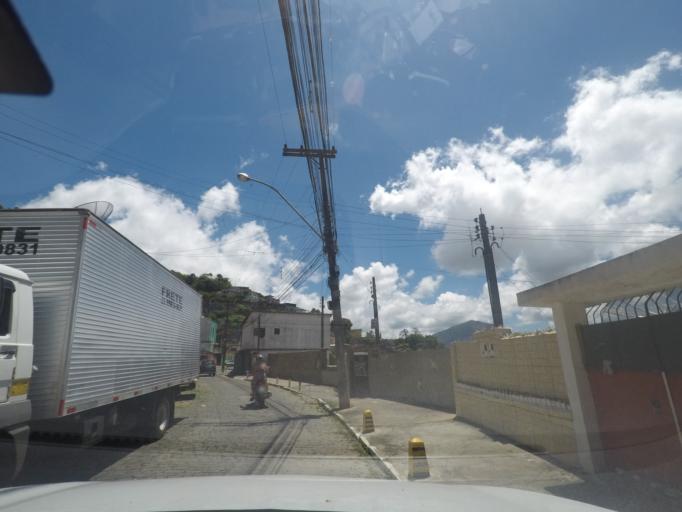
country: BR
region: Rio de Janeiro
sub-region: Teresopolis
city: Teresopolis
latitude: -22.4224
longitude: -42.9868
